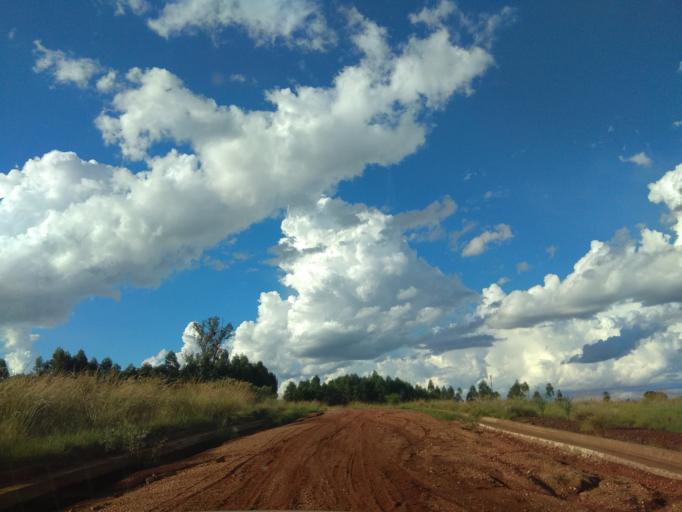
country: AR
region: Misiones
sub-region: Departamento de Candelaria
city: Candelaria
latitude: -27.4823
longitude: -55.7519
